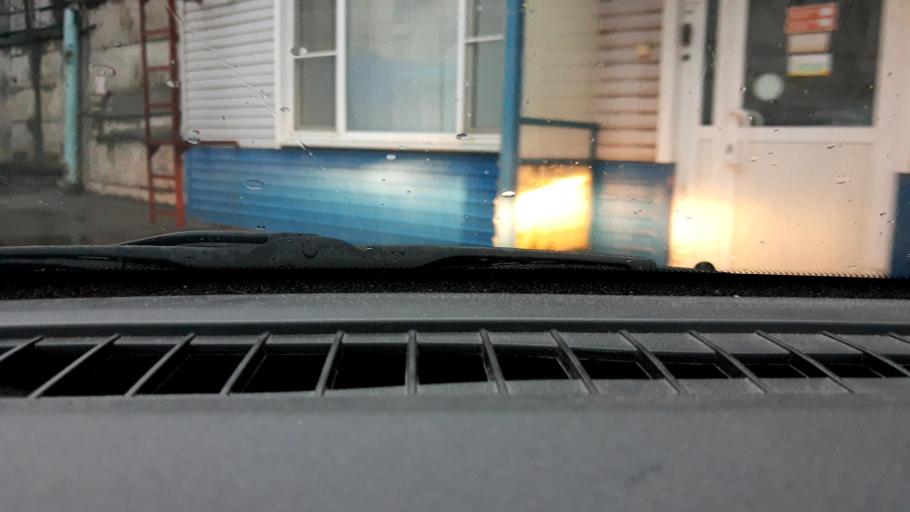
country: RU
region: Nizjnij Novgorod
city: Gorbatovka
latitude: 56.2537
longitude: 43.8755
